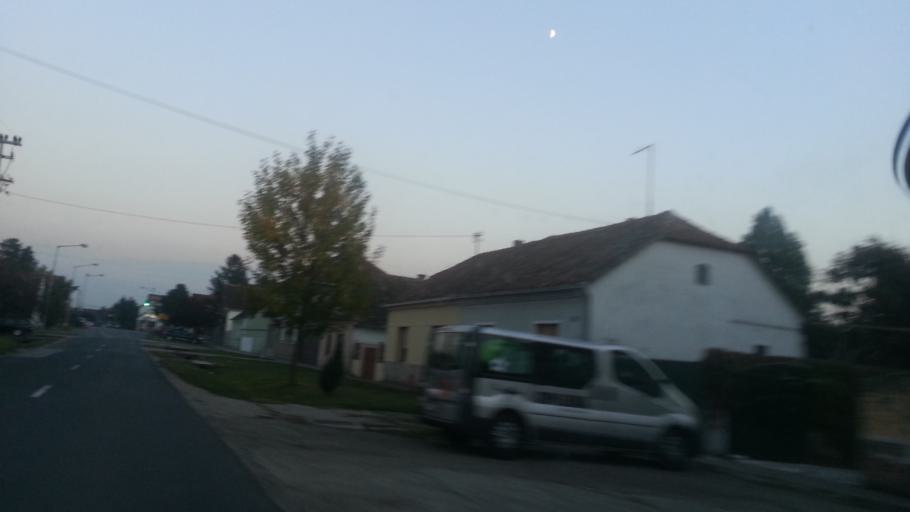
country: RS
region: Autonomna Pokrajina Vojvodina
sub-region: Sremski Okrug
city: Ingija
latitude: 45.0450
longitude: 20.0740
